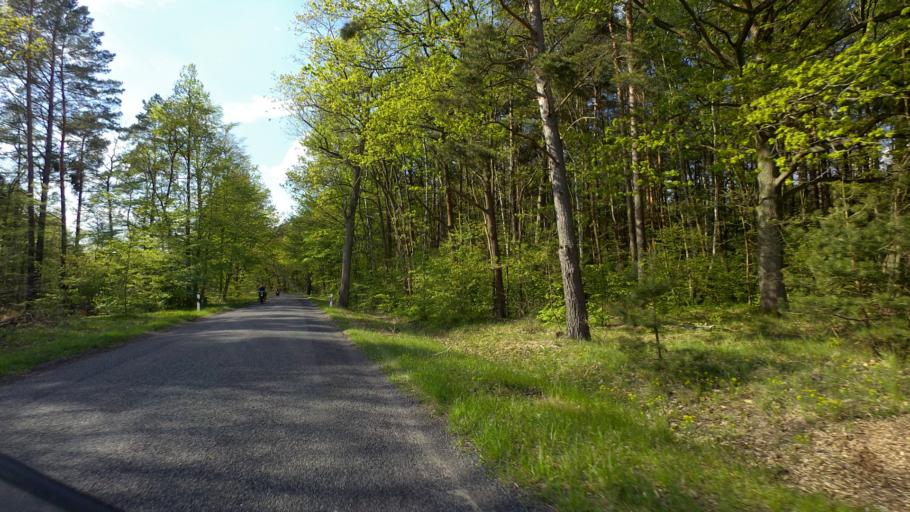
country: DE
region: Brandenburg
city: Templin
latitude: 53.0064
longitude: 13.4628
